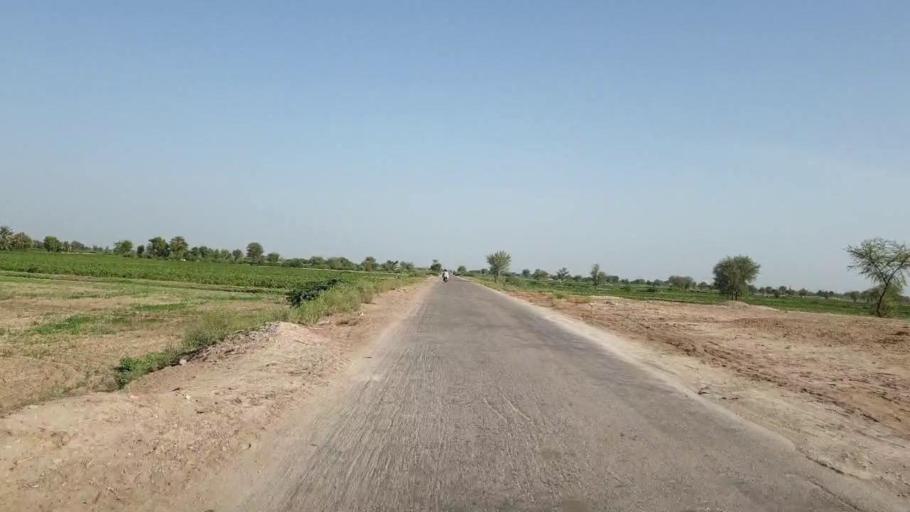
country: PK
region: Sindh
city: Nawabshah
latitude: 26.1342
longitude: 68.4546
